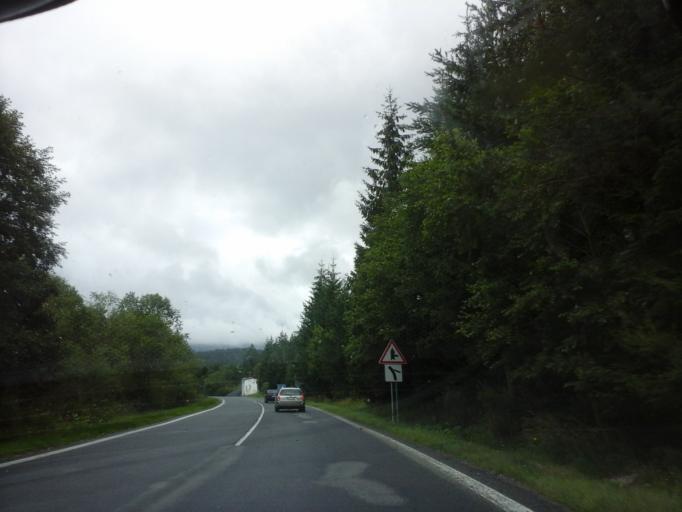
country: SK
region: Kosicky
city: Dobsina
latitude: 48.8858
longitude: 20.2431
